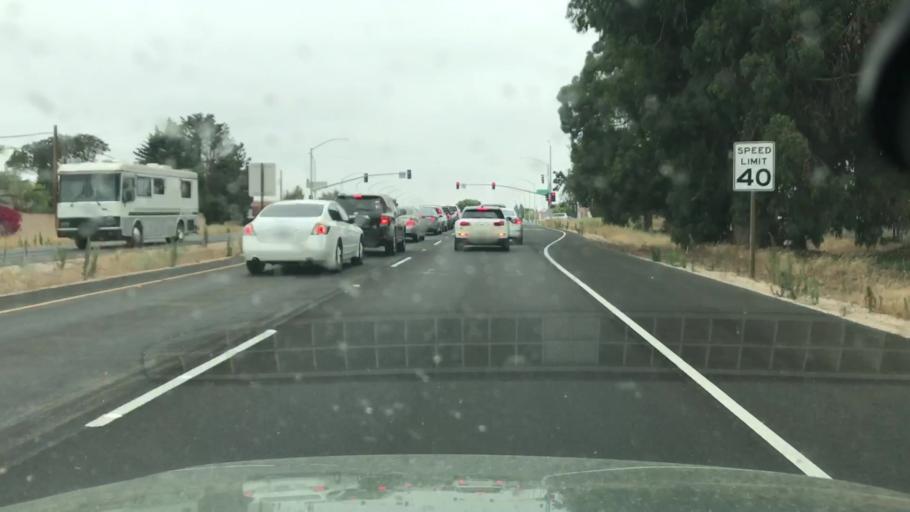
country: US
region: California
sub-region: Santa Barbara County
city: Santa Maria
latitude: 34.9117
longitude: -120.4358
